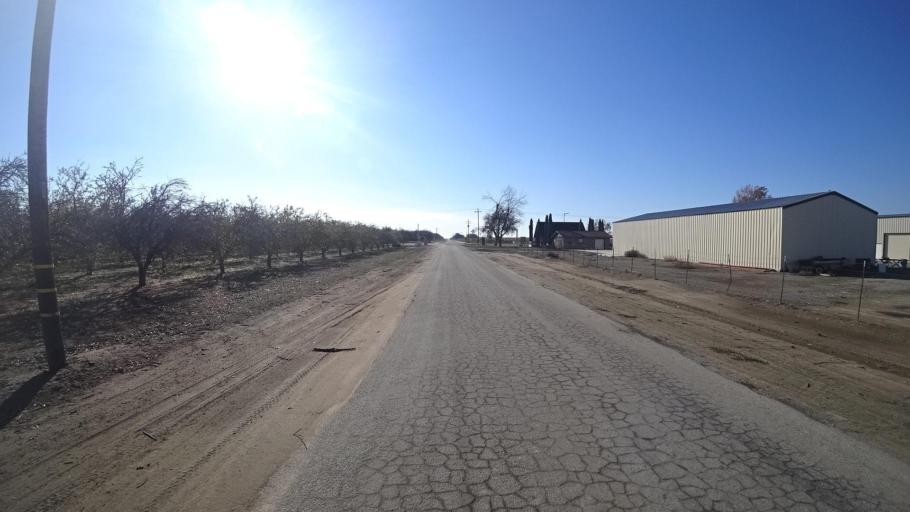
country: US
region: California
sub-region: Kern County
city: McFarland
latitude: 35.6898
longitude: -119.2673
